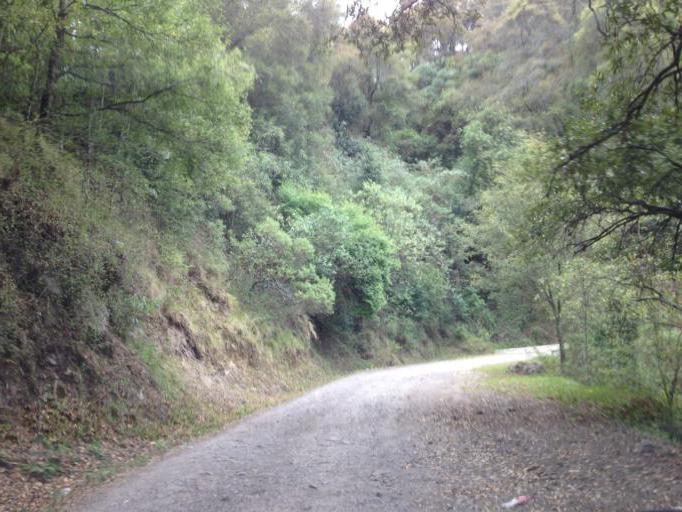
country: MX
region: Hidalgo
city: Mineral del Monte
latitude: 20.2091
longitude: -98.6757
